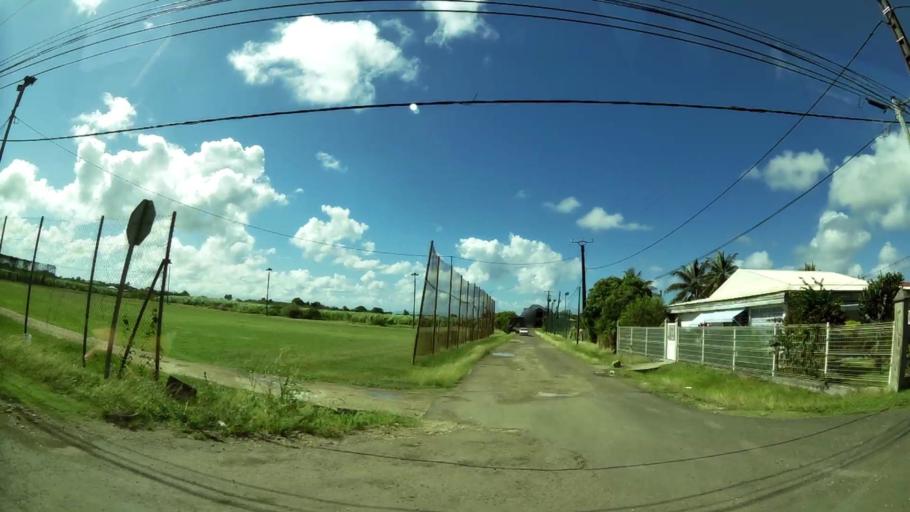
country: GP
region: Guadeloupe
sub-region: Guadeloupe
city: Petit-Canal
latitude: 16.3970
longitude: -61.4631
